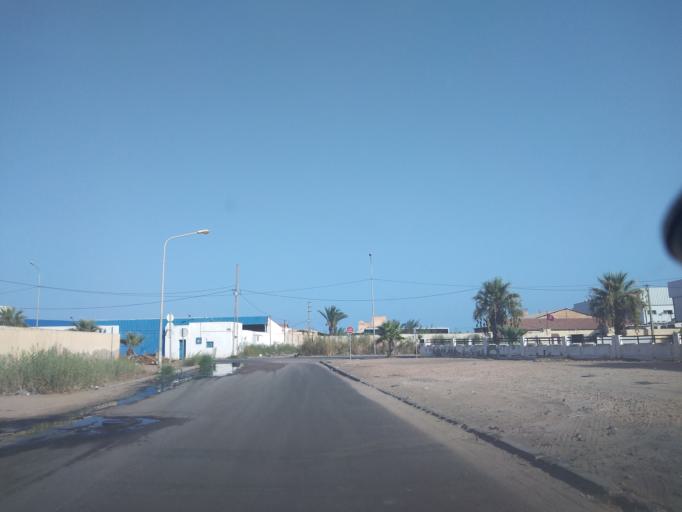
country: TN
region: Safaqis
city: Sfax
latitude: 34.7441
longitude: 10.7666
